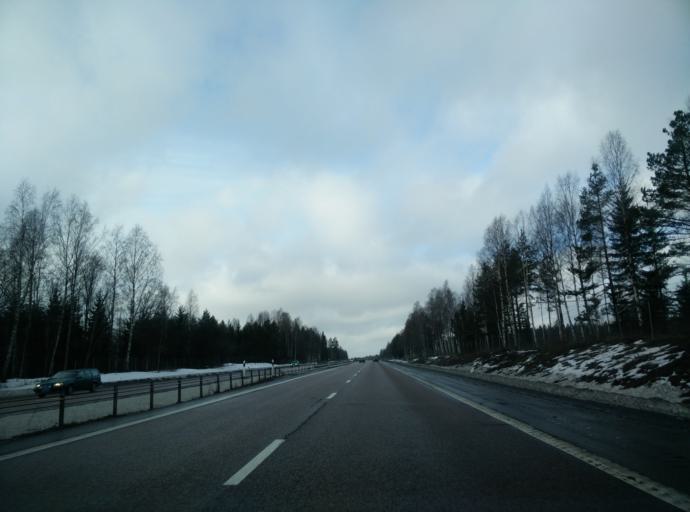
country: SE
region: Gaevleborg
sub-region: Gavle Kommun
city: Valbo
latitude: 60.6280
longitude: 16.9414
